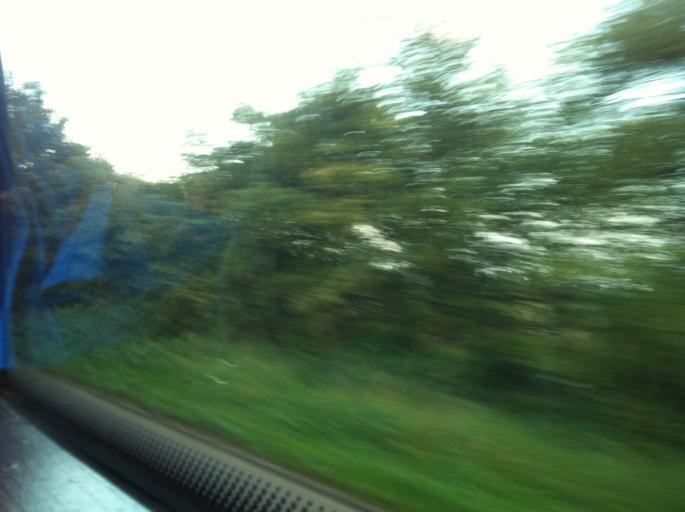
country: GB
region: England
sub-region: Norfolk
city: Bowthorpe
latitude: 52.6262
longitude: 1.2253
